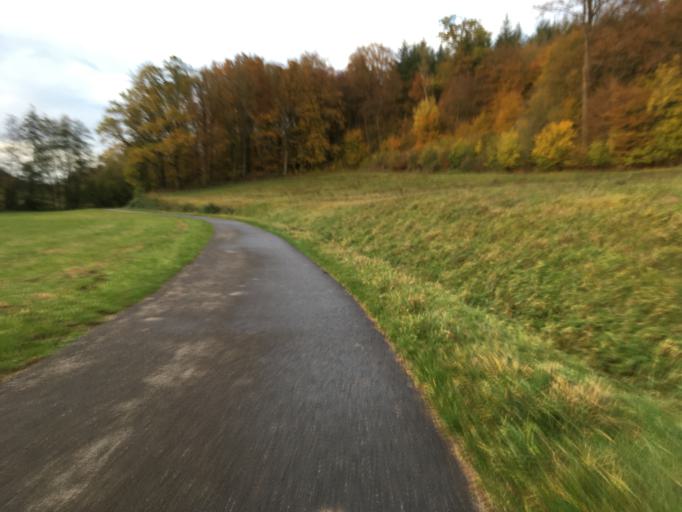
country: DE
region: Baden-Wuerttemberg
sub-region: Regierungsbezirk Stuttgart
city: Jagsthausen
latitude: 49.3756
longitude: 9.4997
